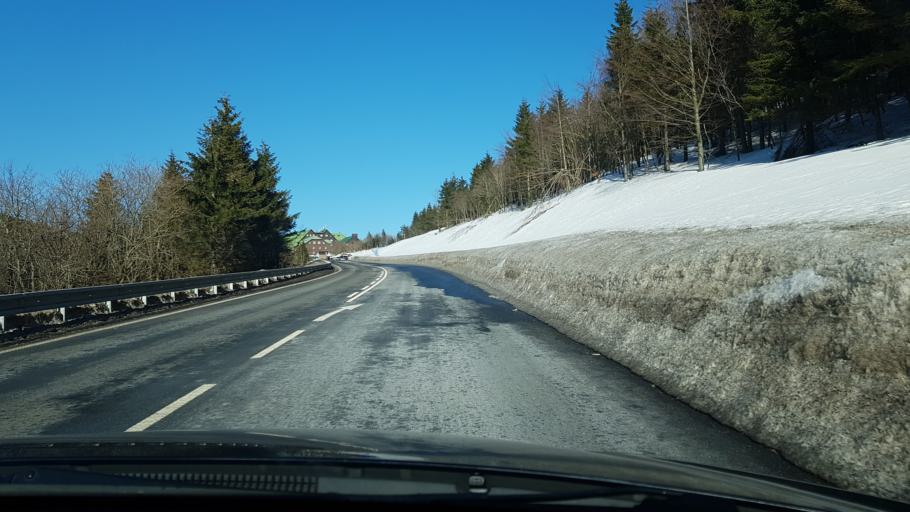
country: CZ
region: Olomoucky
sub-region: Okres Sumperk
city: Loucna nad Desnou
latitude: 50.1214
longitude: 17.1503
